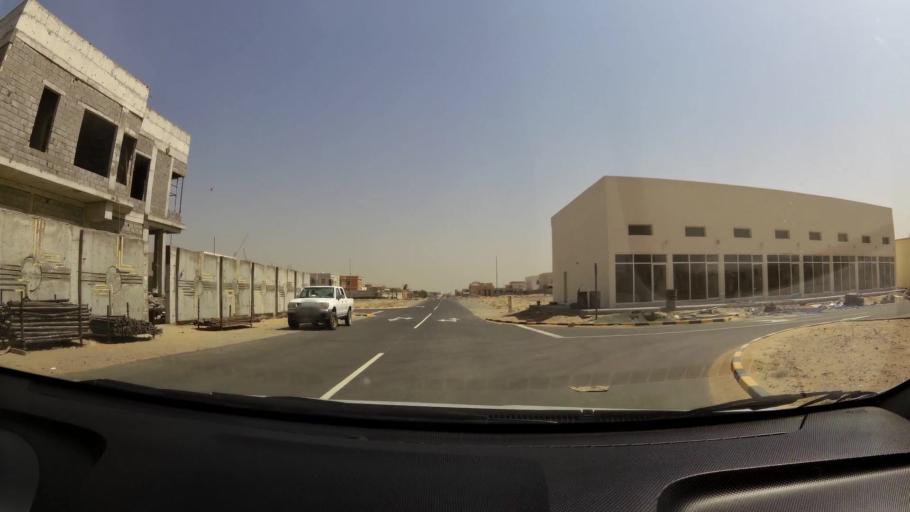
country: AE
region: Ajman
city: Ajman
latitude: 25.4049
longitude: 55.5329
